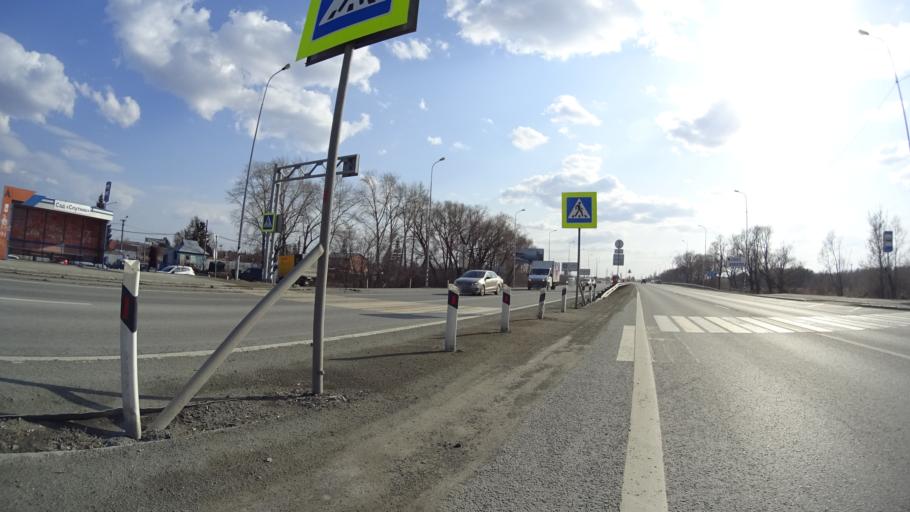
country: RU
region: Chelyabinsk
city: Novosineglazovskiy
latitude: 55.0936
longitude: 61.3310
